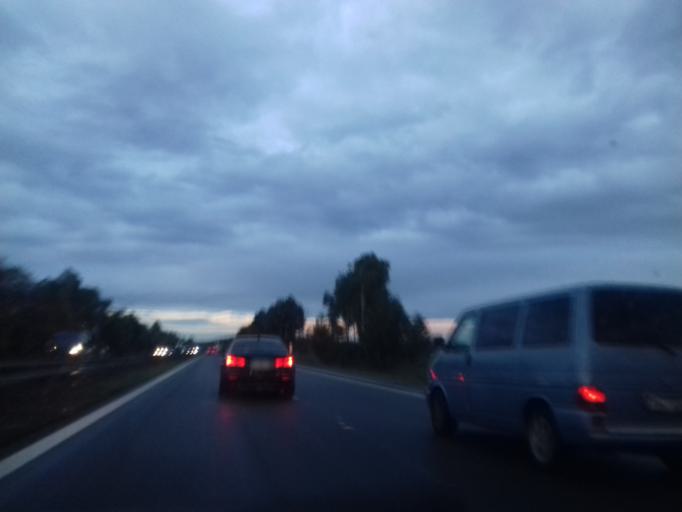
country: CZ
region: Central Bohemia
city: Zruc nad Sazavou
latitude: 49.6690
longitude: 15.1184
